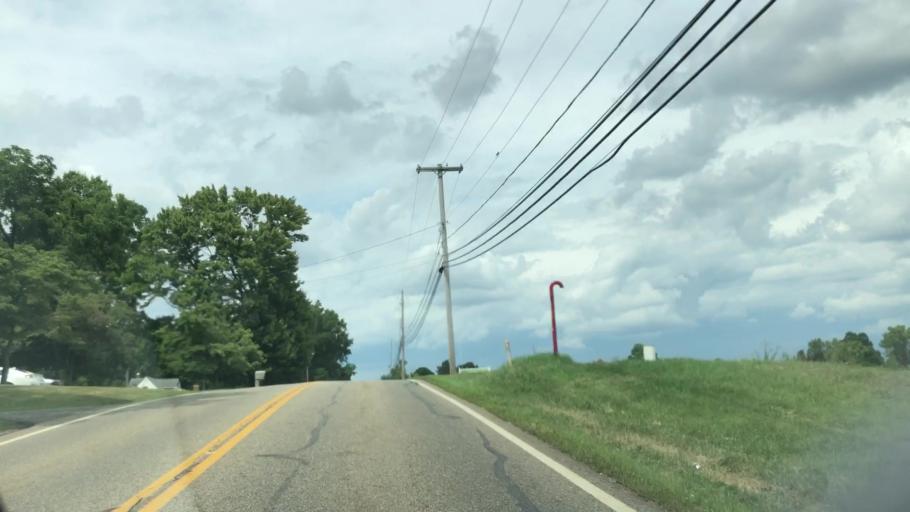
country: US
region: Ohio
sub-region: Stark County
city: North Canton
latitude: 40.8708
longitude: -81.4606
